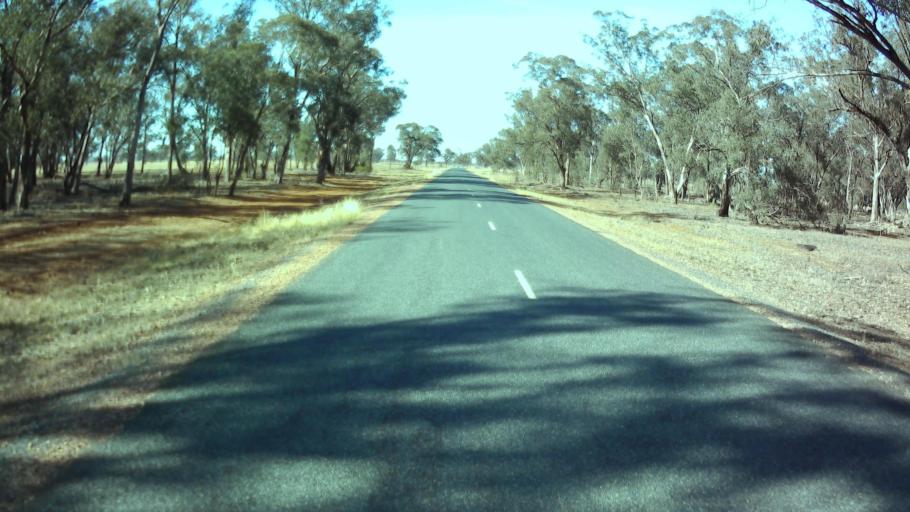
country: AU
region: New South Wales
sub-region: Weddin
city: Grenfell
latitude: -34.0662
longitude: 147.9068
